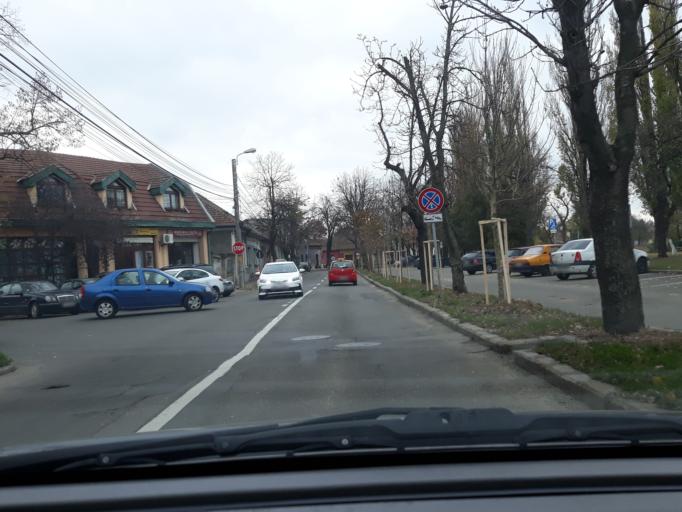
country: RO
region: Bihor
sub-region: Comuna Biharea
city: Oradea
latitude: 47.0646
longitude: 21.9236
